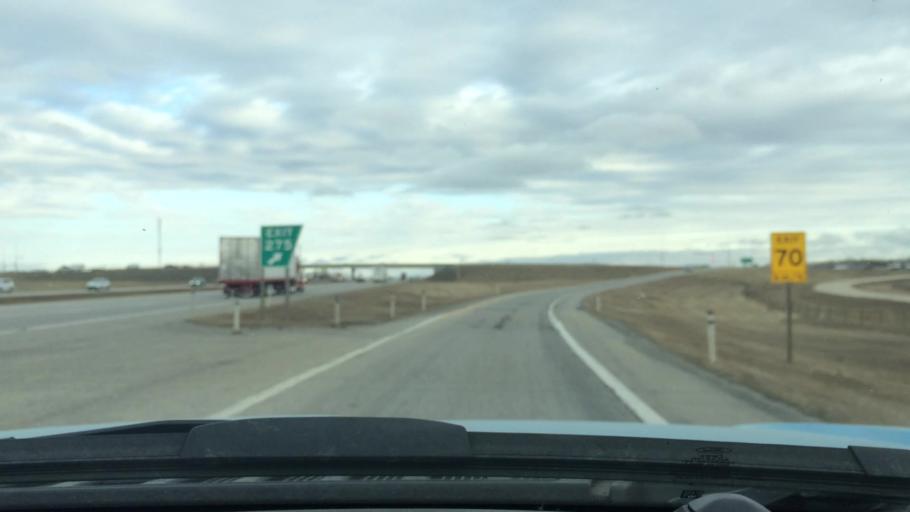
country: CA
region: Alberta
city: Airdrie
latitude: 51.2091
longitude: -114.0011
